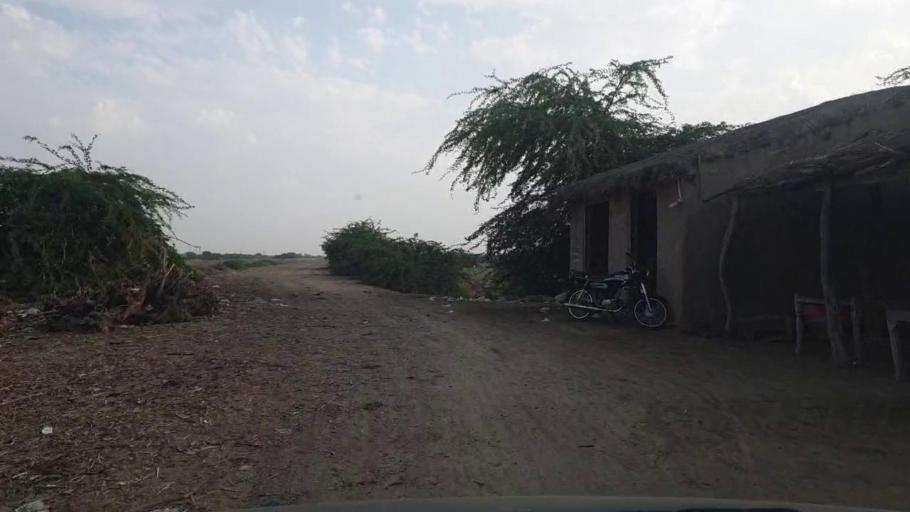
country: PK
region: Sindh
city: Badin
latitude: 24.5287
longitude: 68.6791
